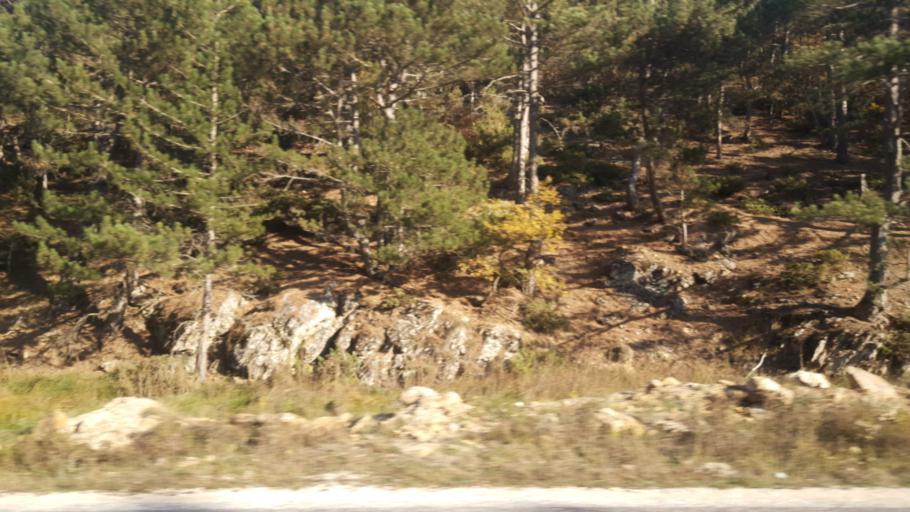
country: TR
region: Afyonkarahisar
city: Ihsaniye
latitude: 39.1041
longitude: 30.5811
